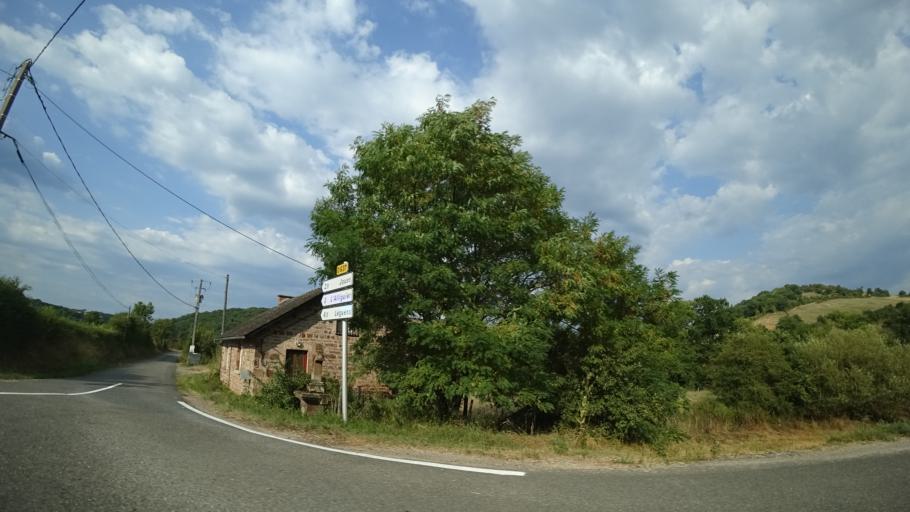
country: FR
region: Midi-Pyrenees
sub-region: Departement de l'Aveyron
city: Saint-Christophe-Vallon
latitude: 44.4941
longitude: 2.3874
